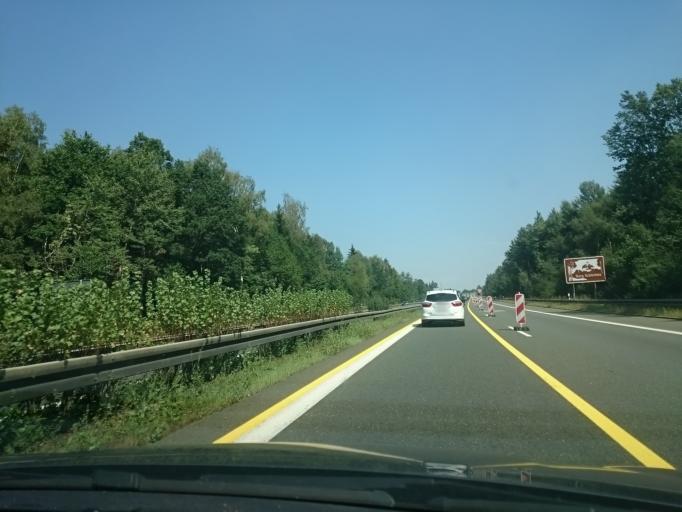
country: DE
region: Saxony
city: Hirschfeld
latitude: 50.6291
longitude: 12.4229
